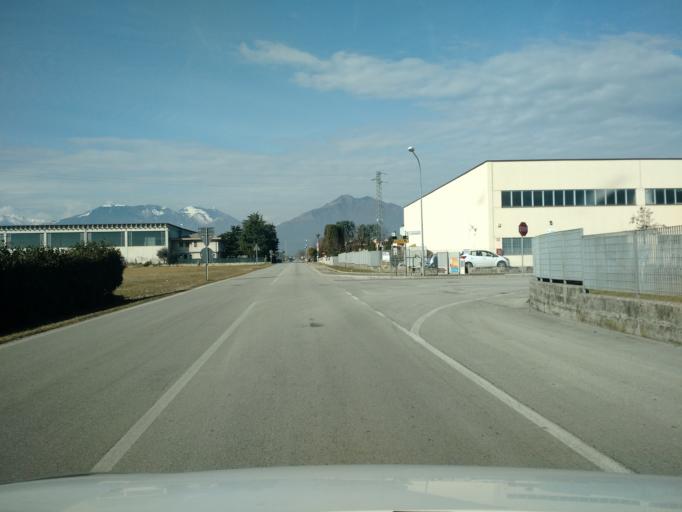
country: IT
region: Veneto
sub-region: Provincia di Vicenza
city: Marano Vicentino
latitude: 45.6768
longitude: 11.4572
